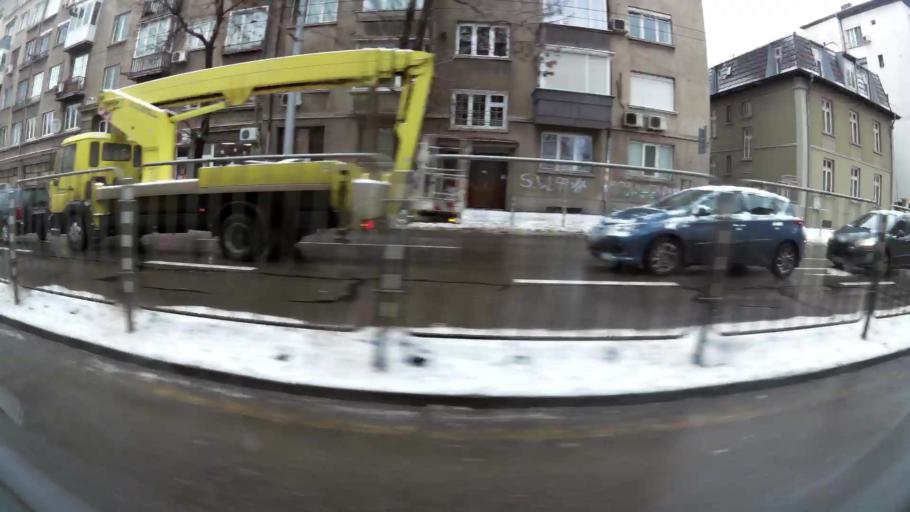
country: BG
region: Sofia-Capital
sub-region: Stolichna Obshtina
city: Sofia
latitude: 42.7007
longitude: 23.3341
